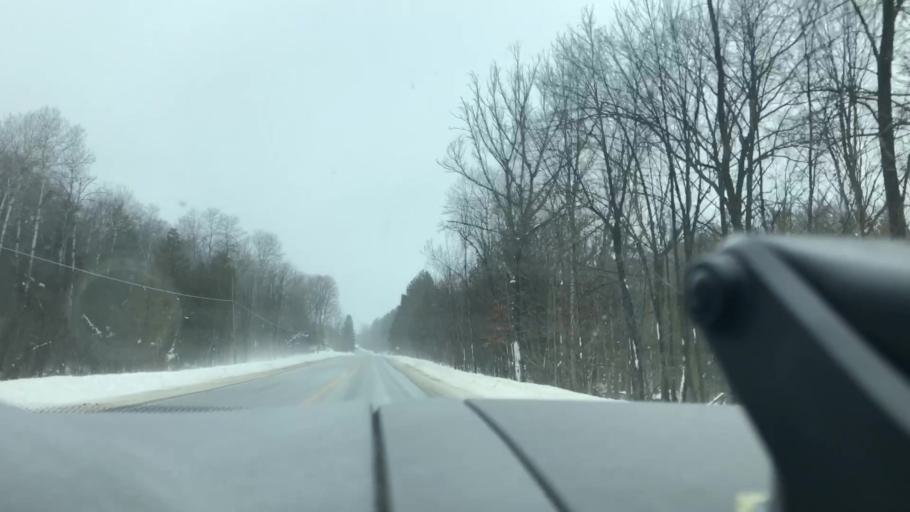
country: US
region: Michigan
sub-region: Charlevoix County
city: East Jordan
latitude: 45.1556
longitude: -85.1522
